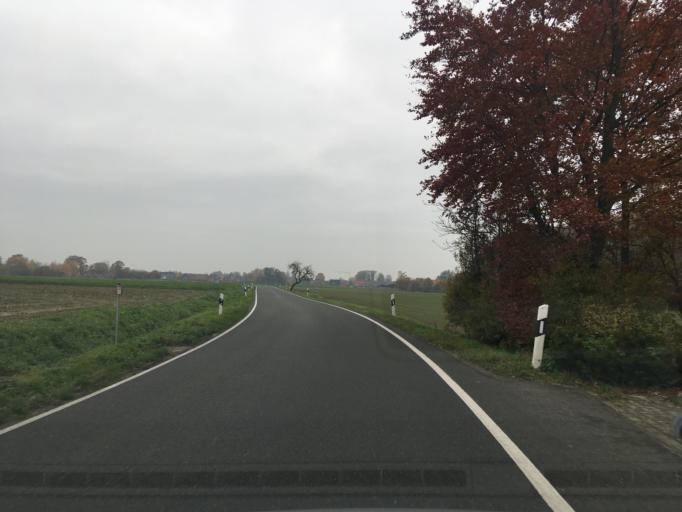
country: DE
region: North Rhine-Westphalia
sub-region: Regierungsbezirk Munster
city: Legden
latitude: 52.0340
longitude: 7.1225
